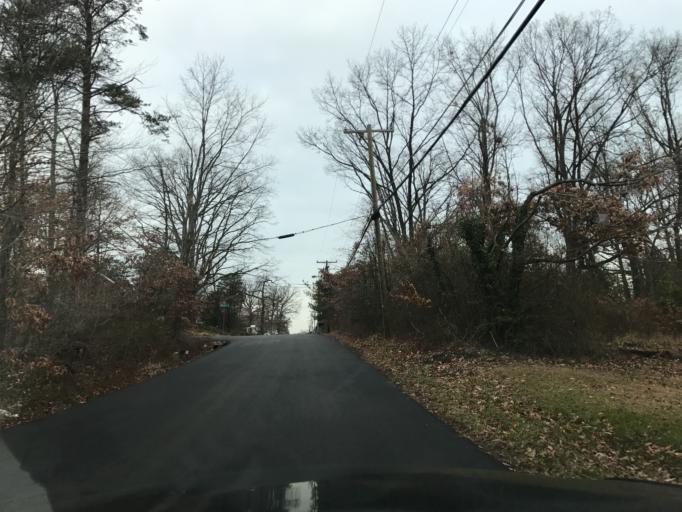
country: US
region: Maryland
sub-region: Baltimore County
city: Overlea
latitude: 39.3502
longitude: -76.5070
